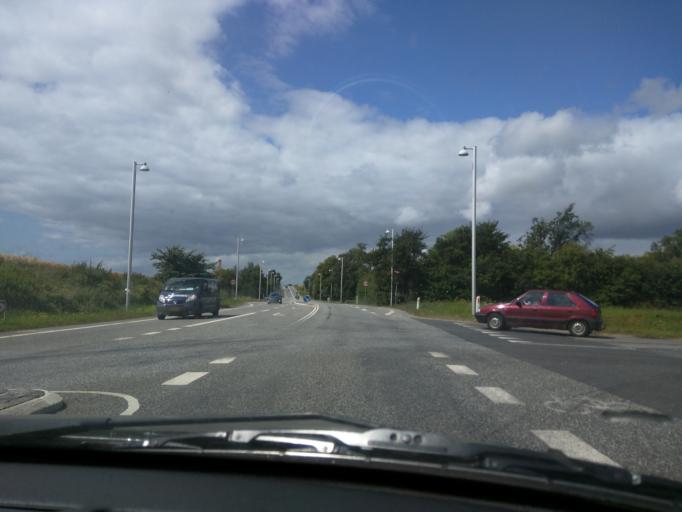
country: DK
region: Zealand
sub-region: Kalundborg Kommune
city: Svebolle
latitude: 55.6717
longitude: 11.2088
